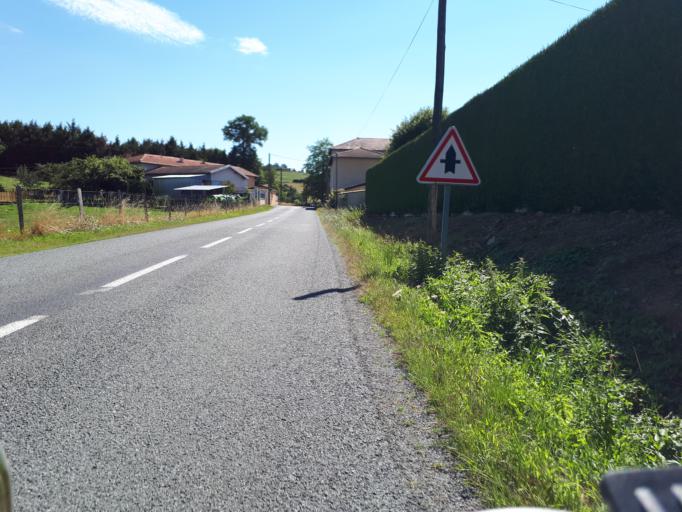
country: FR
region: Rhone-Alpes
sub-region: Departement de la Loire
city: Panissieres
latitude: 45.8062
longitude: 4.3370
